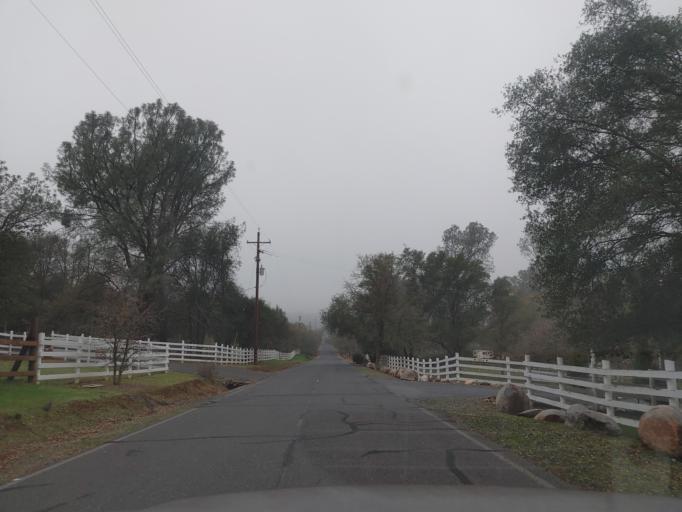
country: US
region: California
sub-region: Calaveras County
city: Copperopolis
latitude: 37.9413
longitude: -120.6128
